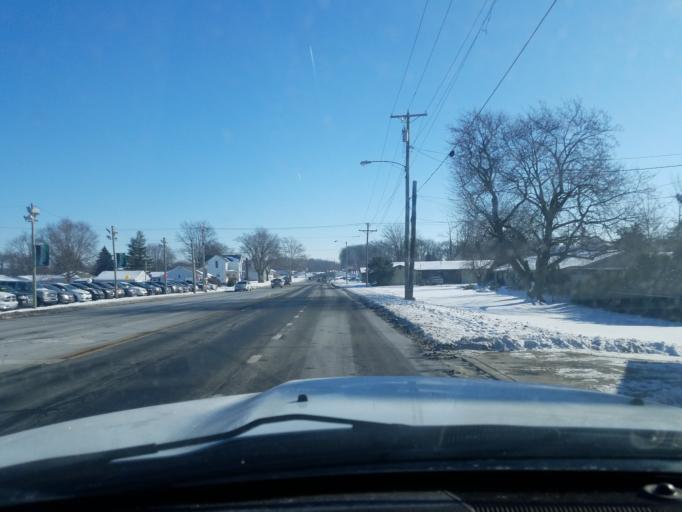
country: US
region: Indiana
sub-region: Noble County
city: Kendallville
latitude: 41.4522
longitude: -85.2603
